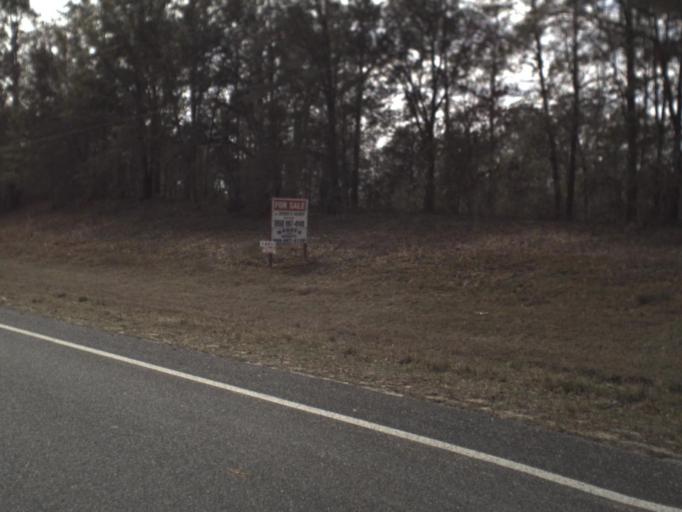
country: US
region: Florida
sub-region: Washington County
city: Chipley
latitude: 30.7325
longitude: -85.3868
